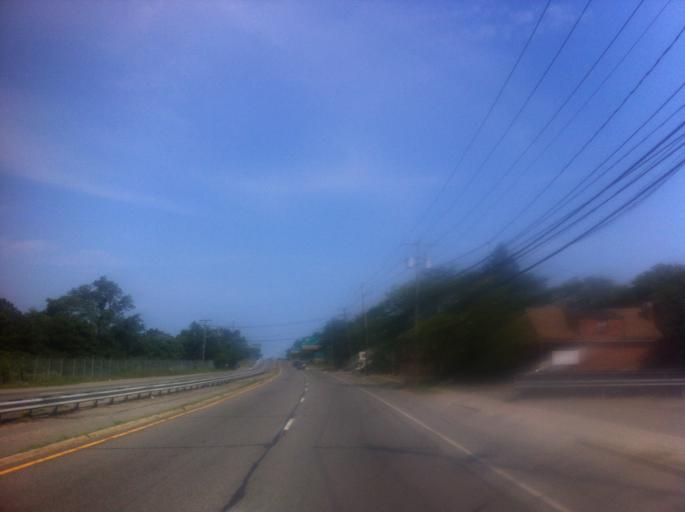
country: US
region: New York
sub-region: Suffolk County
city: East Farmingdale
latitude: 40.7197
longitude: -73.4147
